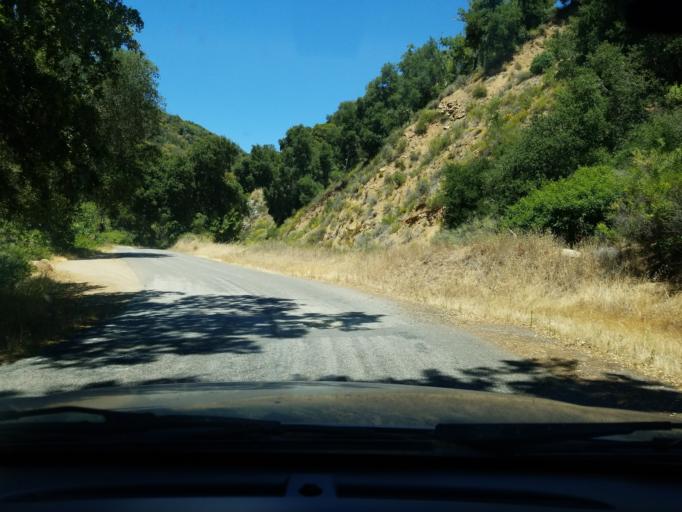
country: US
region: California
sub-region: Monterey County
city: Gonzales
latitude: 36.3581
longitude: -121.5489
